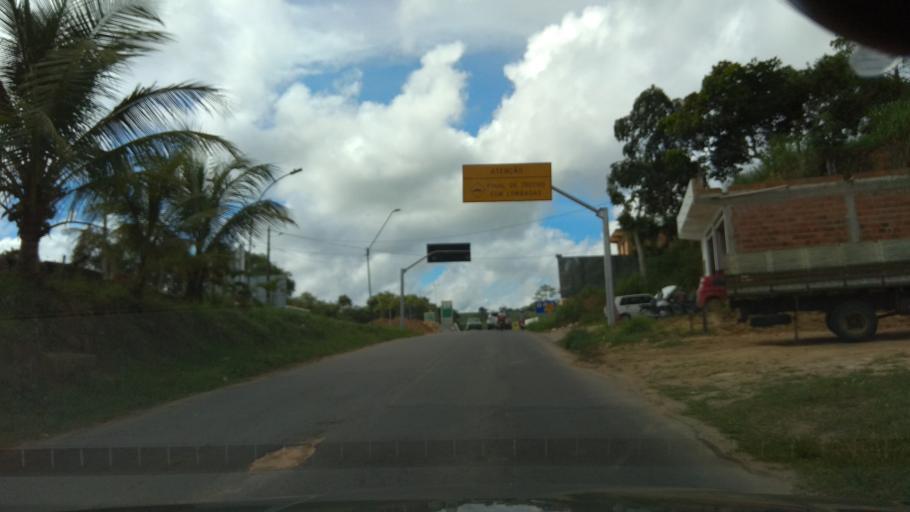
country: BR
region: Bahia
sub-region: Mutuipe
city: Mutuipe
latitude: -13.2283
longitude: -39.4956
